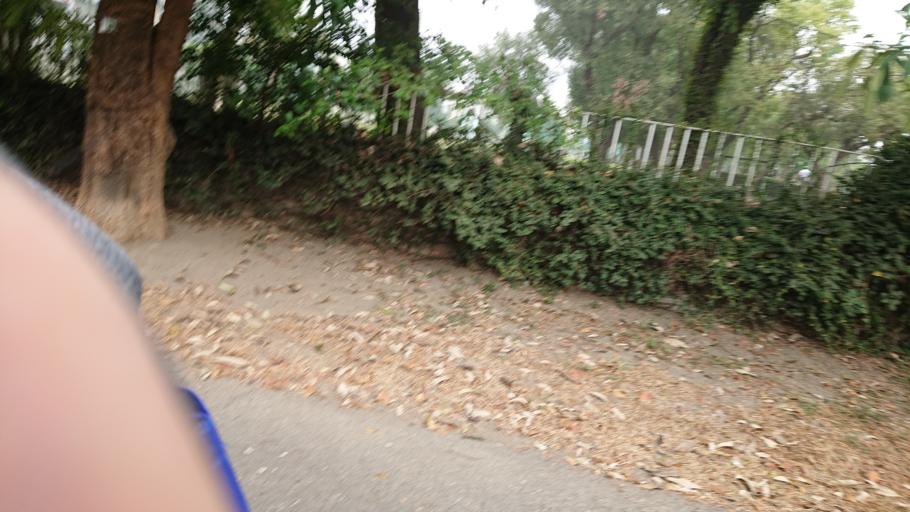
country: TW
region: Kaohsiung
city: Kaohsiung
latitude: 22.7049
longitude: 120.2952
